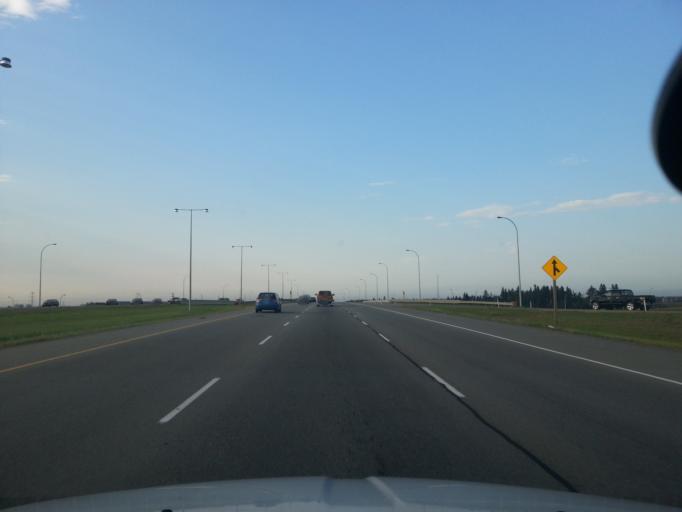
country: CA
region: Alberta
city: St. Albert
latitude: 53.5433
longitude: -113.6595
